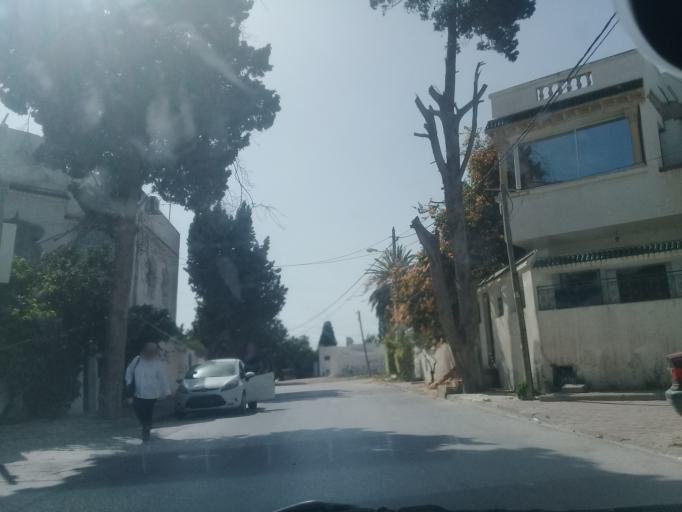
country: TN
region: Tunis
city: Al Marsa
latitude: 36.8879
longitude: 10.3249
